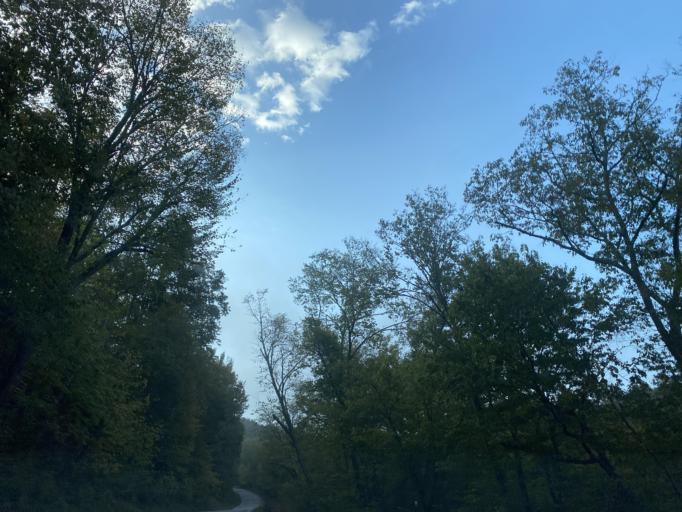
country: US
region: Kentucky
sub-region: Pendleton County
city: Falmouth
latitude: 38.7470
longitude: -84.3178
